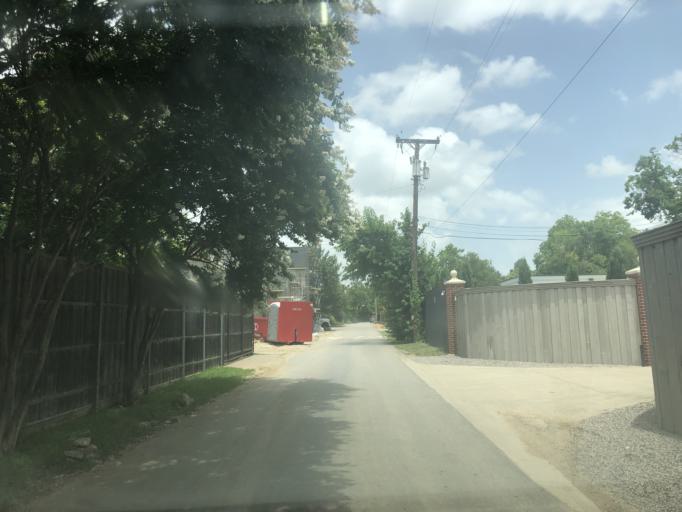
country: US
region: Texas
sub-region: Dallas County
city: University Park
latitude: 32.8544
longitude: -96.8228
